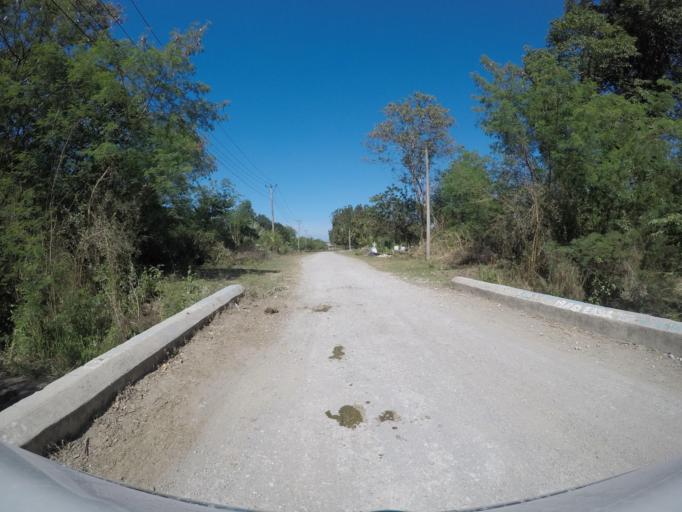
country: TL
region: Viqueque
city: Viqueque
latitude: -8.9731
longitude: 126.0540
